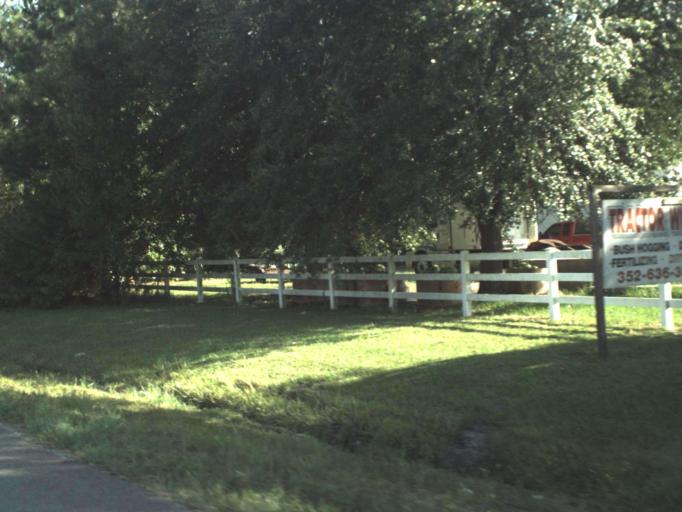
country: US
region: Florida
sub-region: Lake County
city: Clermont
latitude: 28.4031
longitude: -81.8286
